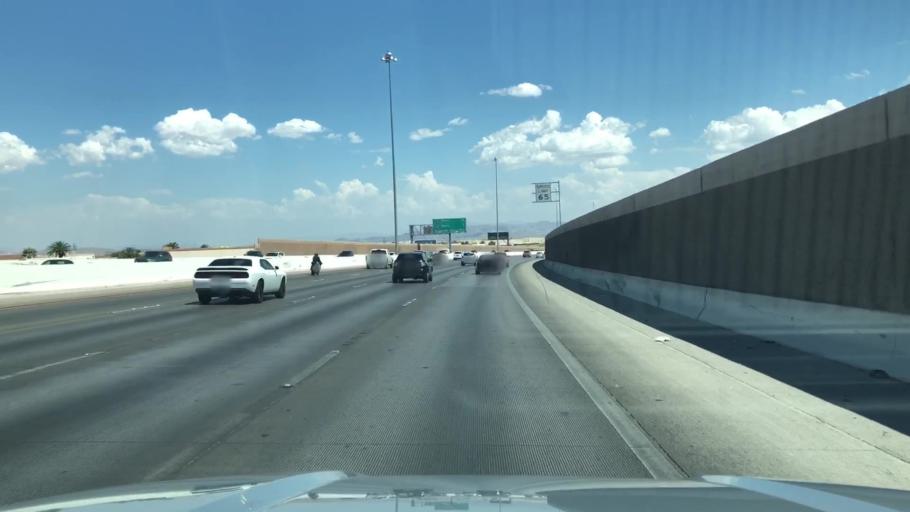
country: US
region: Nevada
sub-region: Clark County
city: Paradise
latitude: 36.0684
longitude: -115.1987
